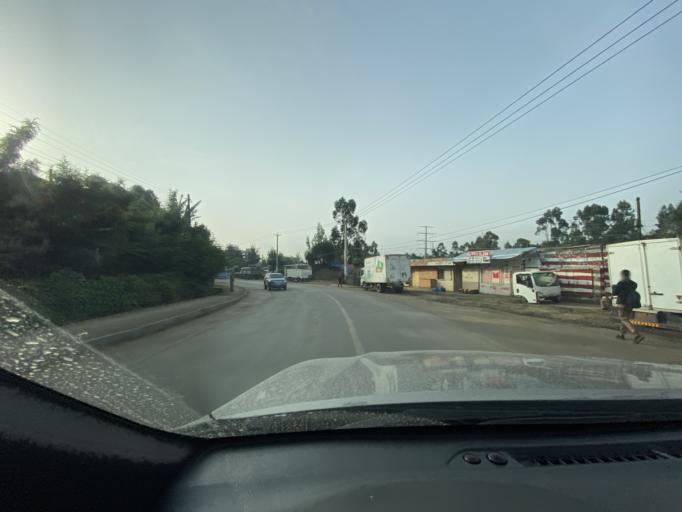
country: ET
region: Adis Abeba
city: Addis Ababa
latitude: 9.0217
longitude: 38.7204
